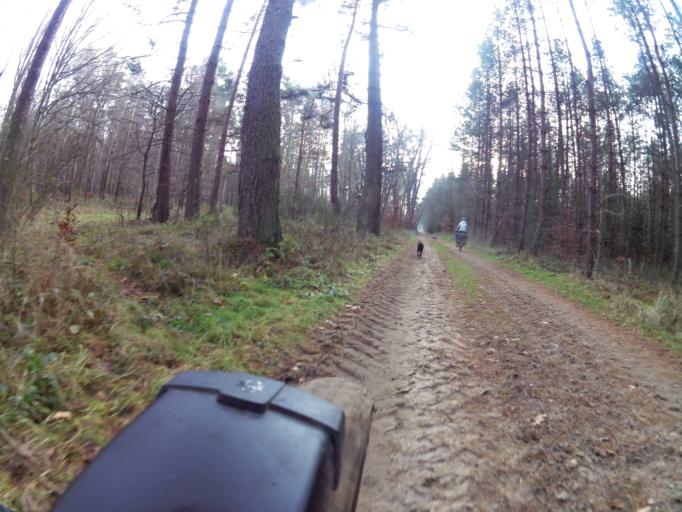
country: PL
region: West Pomeranian Voivodeship
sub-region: Powiat koszalinski
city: Polanow
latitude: 54.1481
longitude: 16.7303
